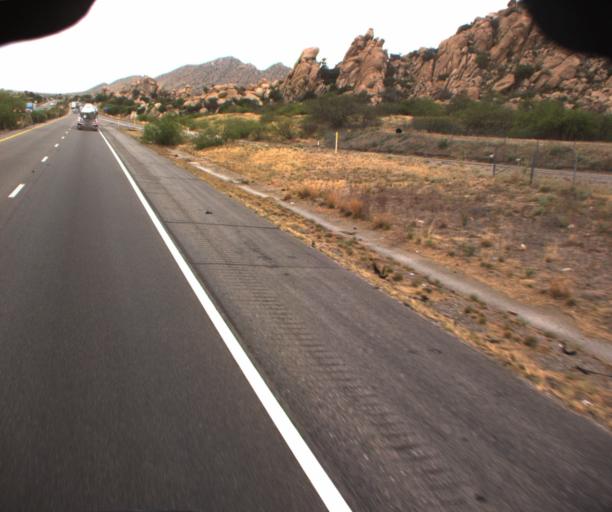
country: US
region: Arizona
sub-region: Cochise County
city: Saint David
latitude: 32.0589
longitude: -110.0787
